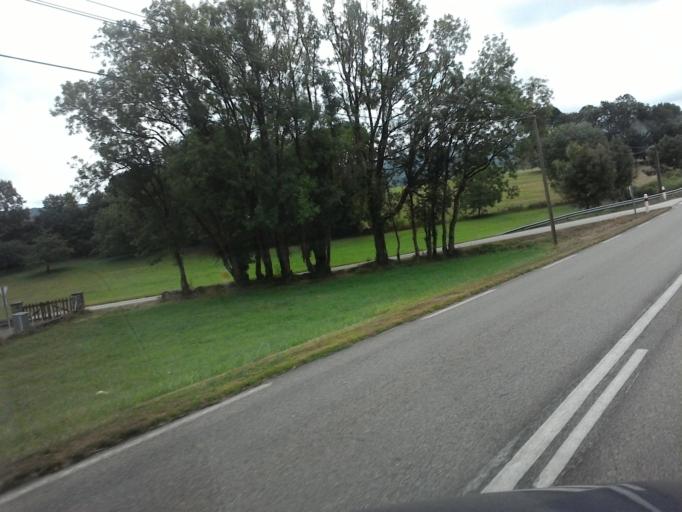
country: FR
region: Franche-Comte
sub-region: Departement du Doubs
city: Quingey
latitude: 47.0691
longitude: 5.8814
